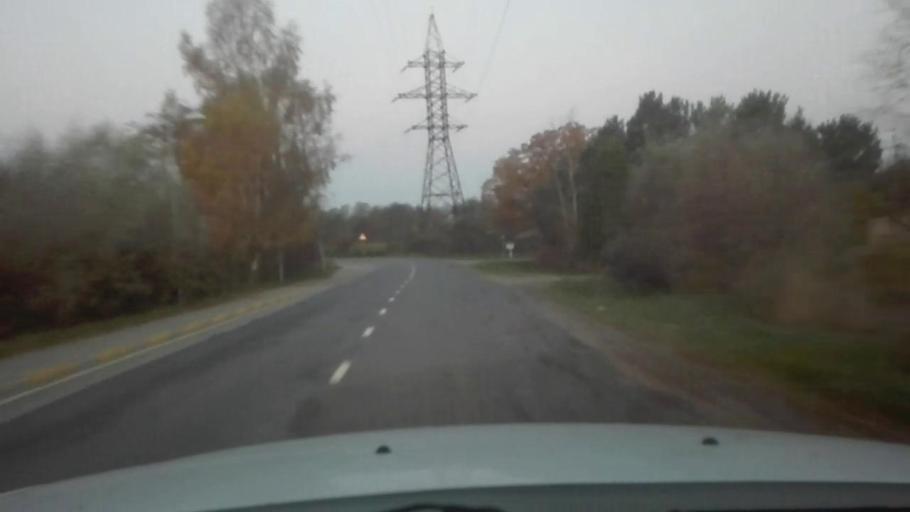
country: EE
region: Harju
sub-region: Maardu linn
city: Maardu
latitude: 59.4792
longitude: 24.9956
